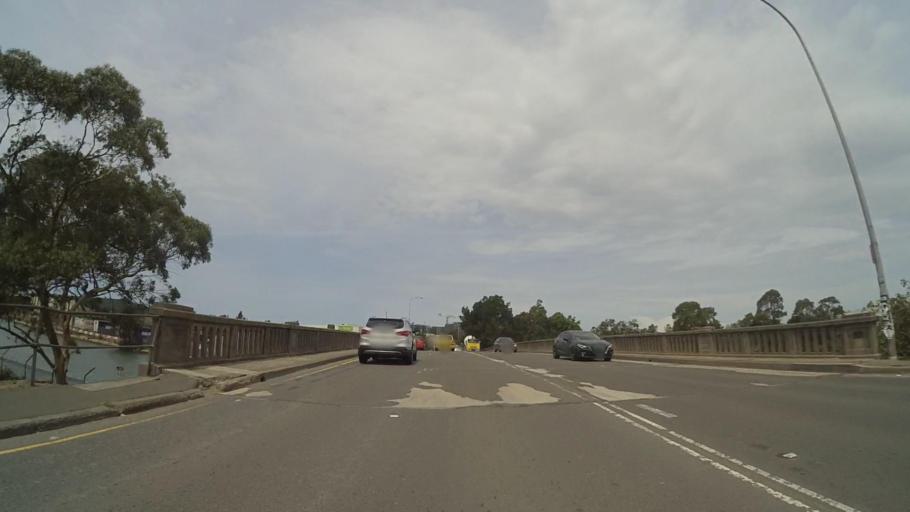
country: AU
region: New South Wales
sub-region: Botany Bay
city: Mascot
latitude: -33.9199
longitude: 151.1789
